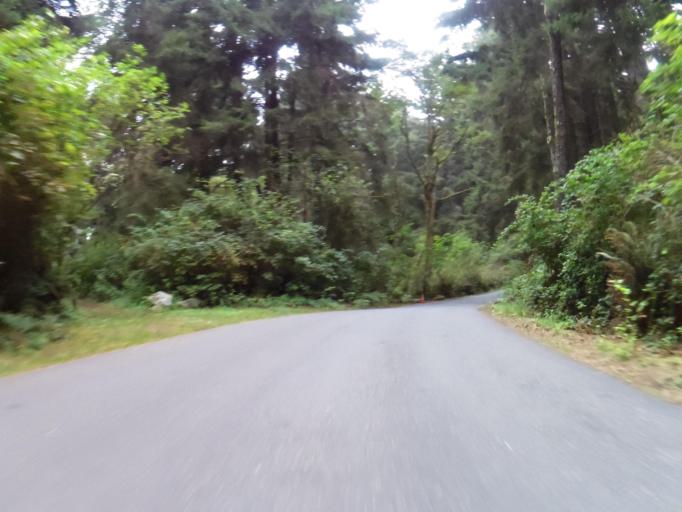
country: US
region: California
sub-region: Humboldt County
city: Westhaven-Moonstone
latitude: 41.1360
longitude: -124.1588
